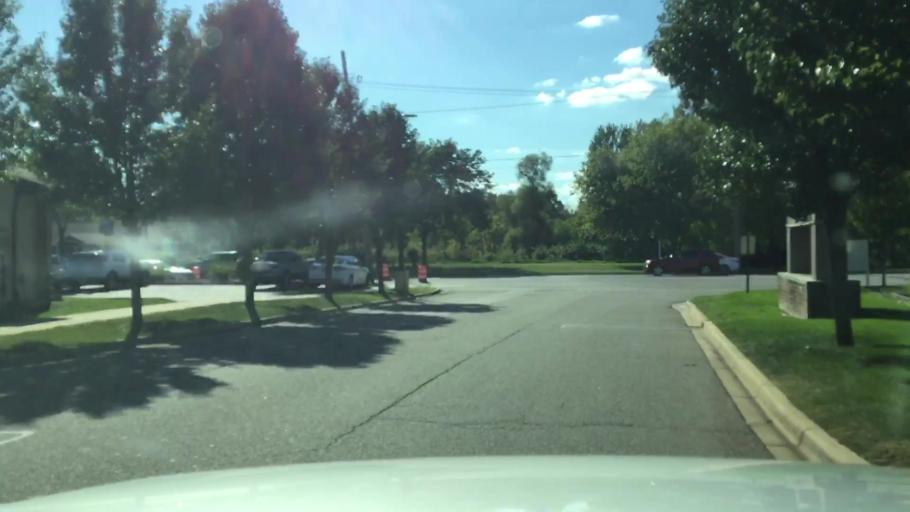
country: US
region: Michigan
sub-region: Kalamazoo County
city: Portage
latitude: 42.2138
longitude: -85.5887
